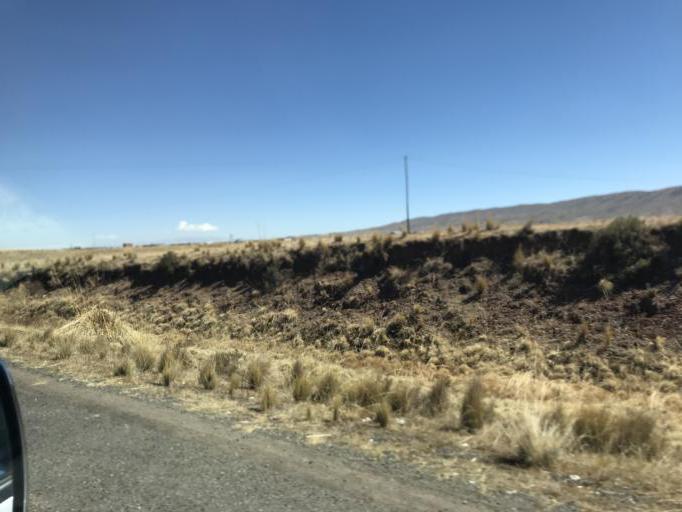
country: BO
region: La Paz
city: Tiahuanaco
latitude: -16.5702
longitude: -68.6678
